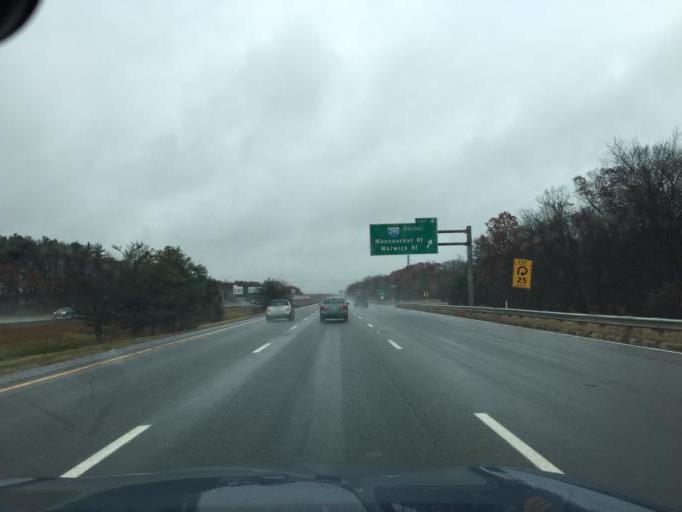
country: US
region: Massachusetts
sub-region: Bristol County
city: Attleboro
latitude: 41.9558
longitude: -71.3036
